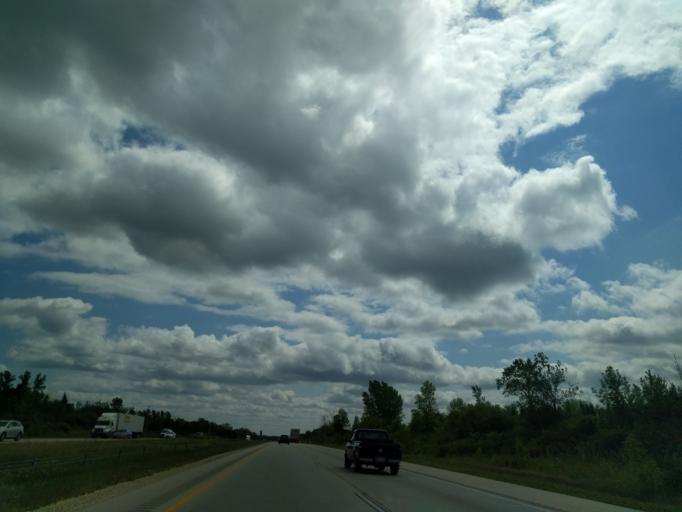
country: US
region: Wisconsin
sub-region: Ozaukee County
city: Thiensville
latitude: 43.2454
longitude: -87.9200
